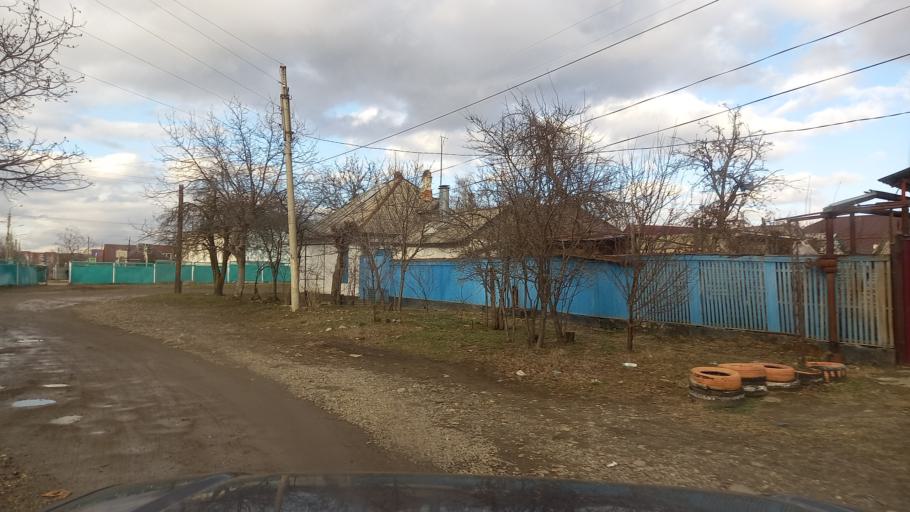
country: RU
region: Adygeya
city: Maykop
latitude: 44.5999
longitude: 40.0808
